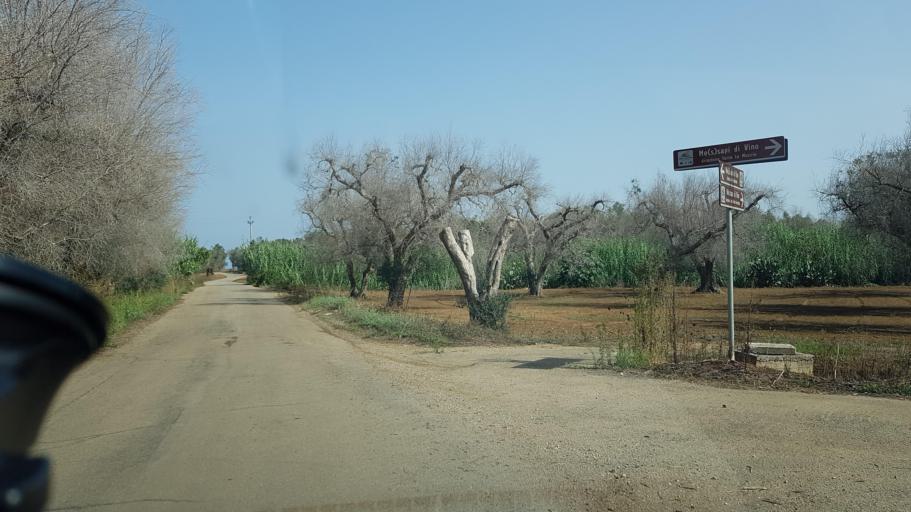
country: IT
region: Apulia
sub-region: Provincia di Brindisi
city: Torchiarolo
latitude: 40.5066
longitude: 18.0596
